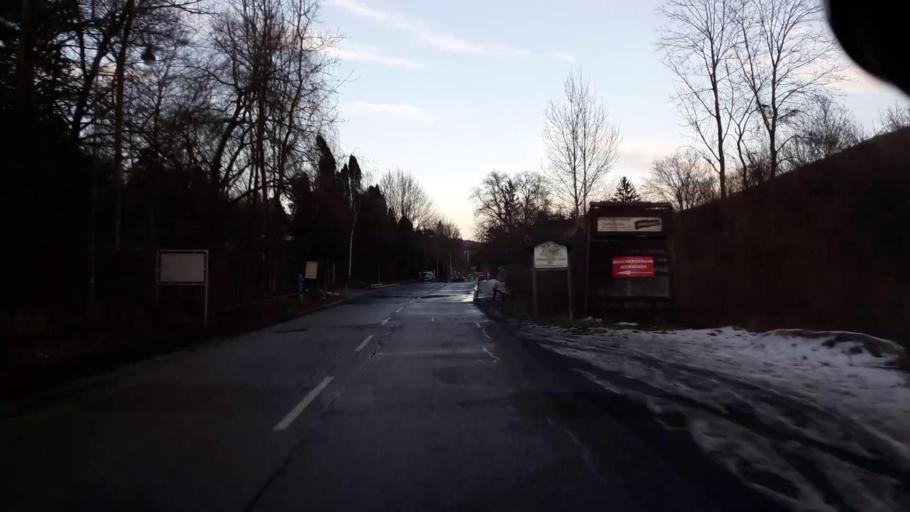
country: AT
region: Lower Austria
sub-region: Politischer Bezirk Wien-Umgebung
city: Klosterneuburg
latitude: 48.2807
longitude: 16.2839
